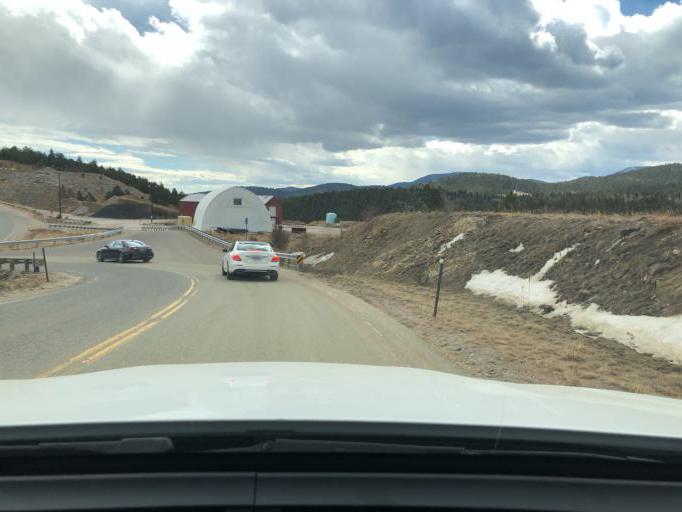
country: US
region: Colorado
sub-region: Gilpin County
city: Central City
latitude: 39.7906
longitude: -105.5173
